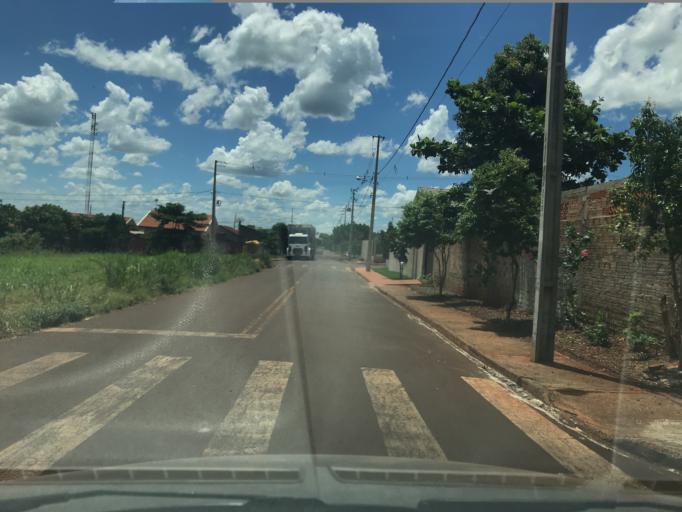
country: BR
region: Parana
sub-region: Palotina
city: Palotina
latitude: -24.2681
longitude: -53.8475
